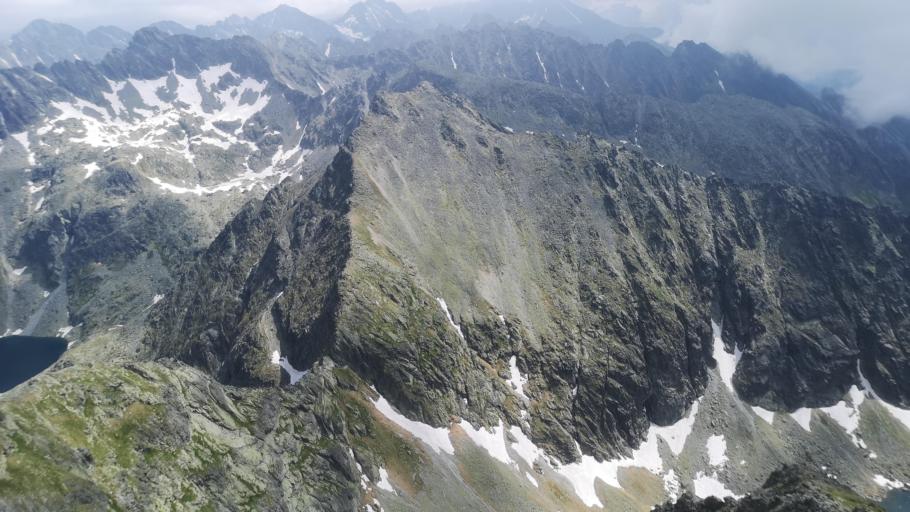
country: SK
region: Presovsky
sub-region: Okres Poprad
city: Strba
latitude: 49.1624
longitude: 20.0006
